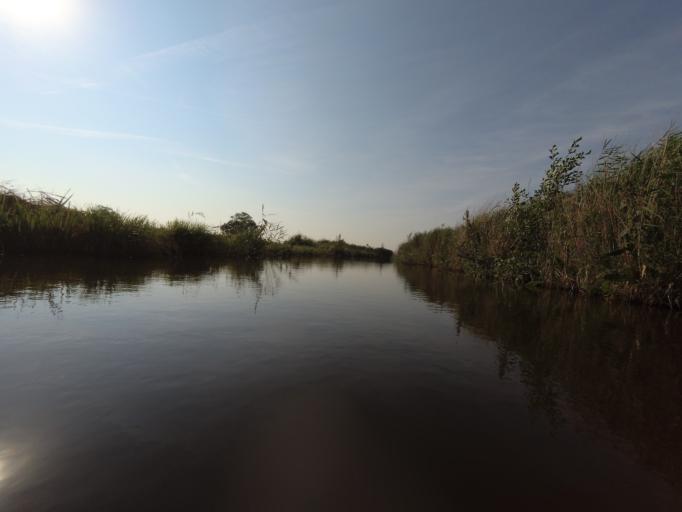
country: NL
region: Overijssel
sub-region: Gemeente Steenwijkerland
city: Wanneperveen
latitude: 52.6705
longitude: 6.0756
